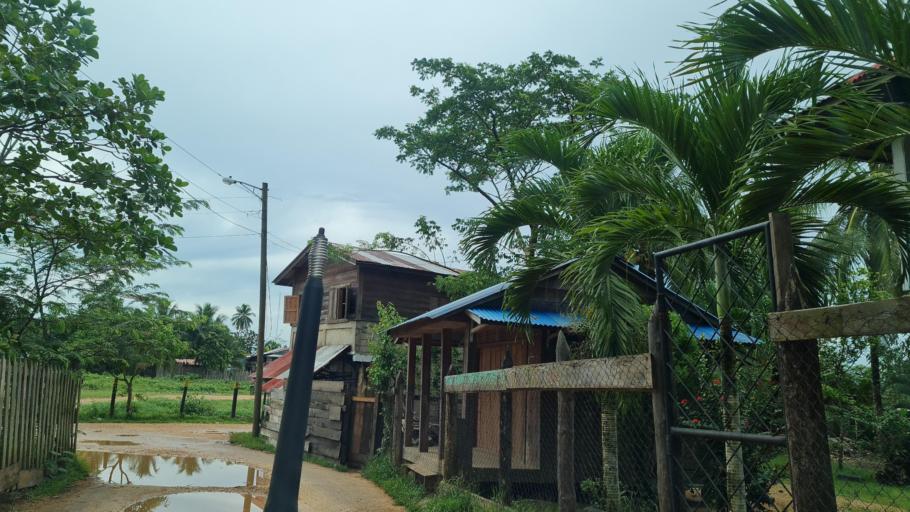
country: NI
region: Atlantico Norte (RAAN)
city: Waspam
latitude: 14.7380
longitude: -83.9702
